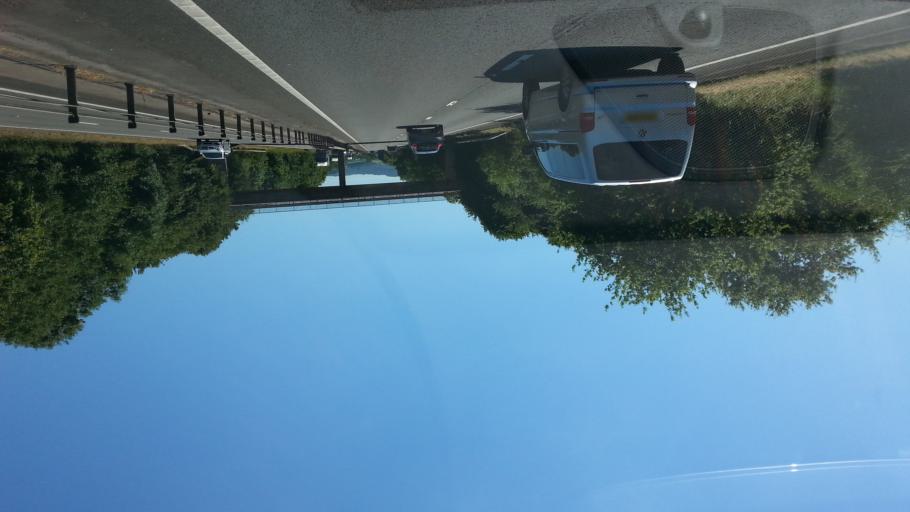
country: GB
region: Wales
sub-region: Monmouthshire
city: Llangwm
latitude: 51.7452
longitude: -2.8417
